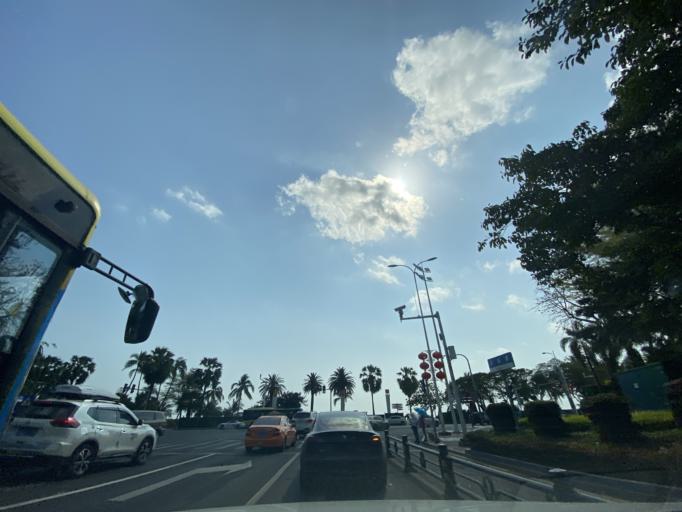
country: CN
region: Hainan
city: Sanya
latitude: 18.2616
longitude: 109.4907
